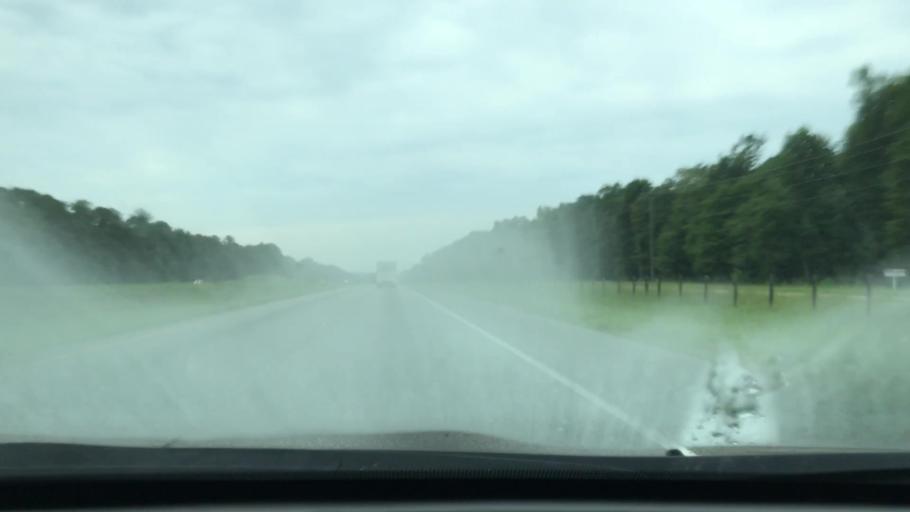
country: US
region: South Carolina
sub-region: Jasper County
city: Ridgeland
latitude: 32.5574
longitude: -80.9454
